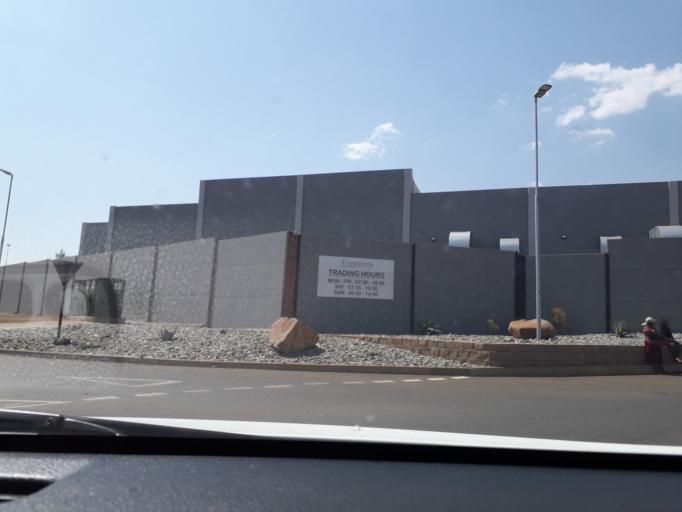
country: ZA
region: Gauteng
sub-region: Ekurhuleni Metropolitan Municipality
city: Tembisa
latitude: -26.0364
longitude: 28.2563
